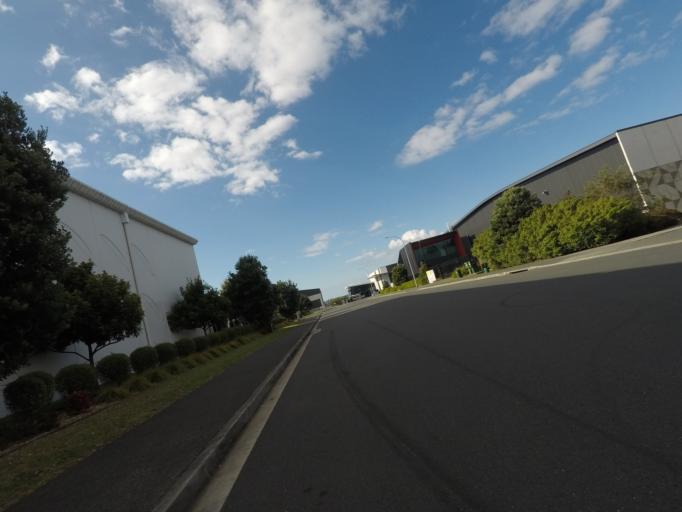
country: NZ
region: Auckland
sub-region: Auckland
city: Rosebank
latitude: -36.8827
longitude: 174.6833
